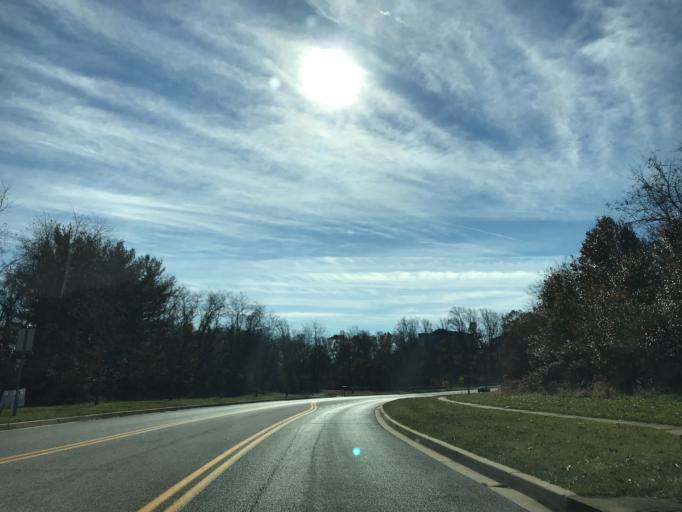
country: US
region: Maryland
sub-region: Howard County
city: West Elkridge
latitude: 39.2074
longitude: -76.7605
